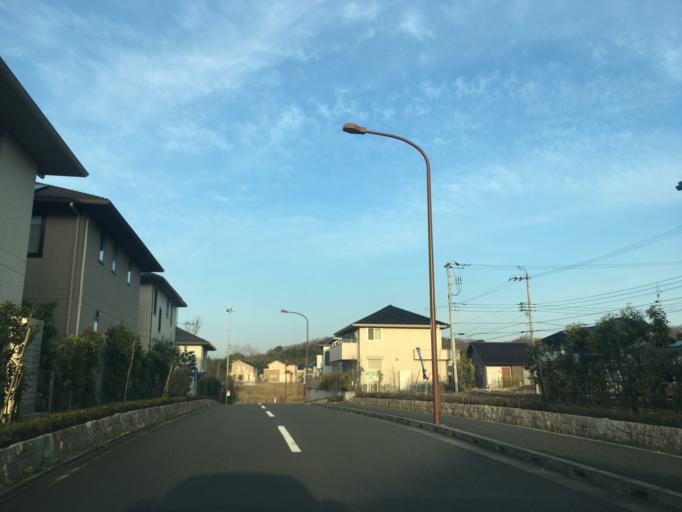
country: JP
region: Tokyo
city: Hino
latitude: 35.6339
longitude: 139.3998
